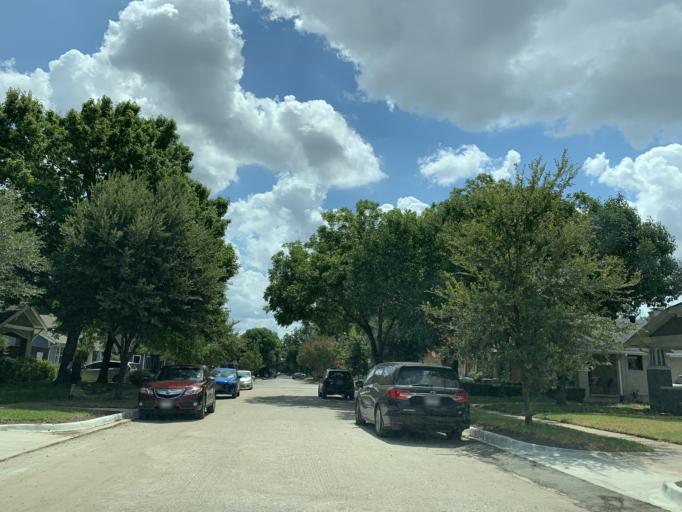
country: US
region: Texas
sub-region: Dallas County
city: Cockrell Hill
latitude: 32.7515
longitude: -96.8452
